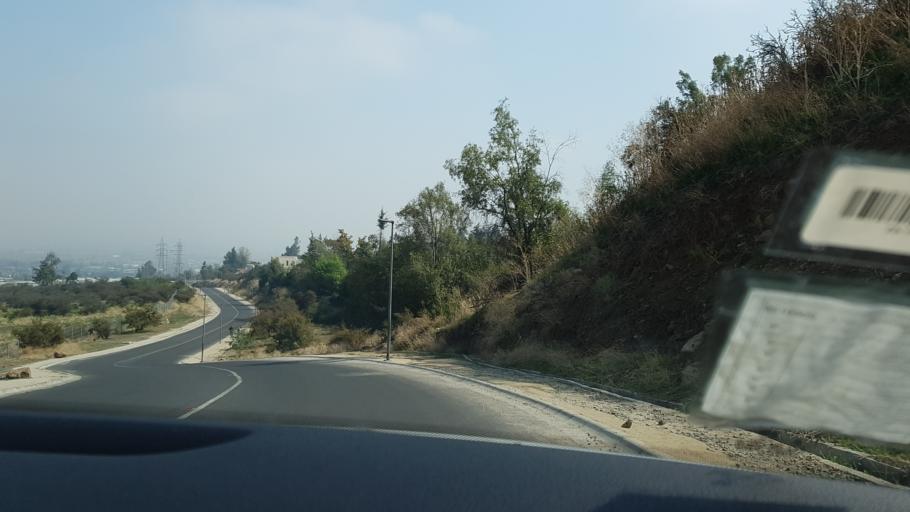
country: CL
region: Santiago Metropolitan
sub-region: Provincia de Santiago
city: Villa Presidente Frei, Nunoa, Santiago, Chile
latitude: -33.4808
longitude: -70.5190
